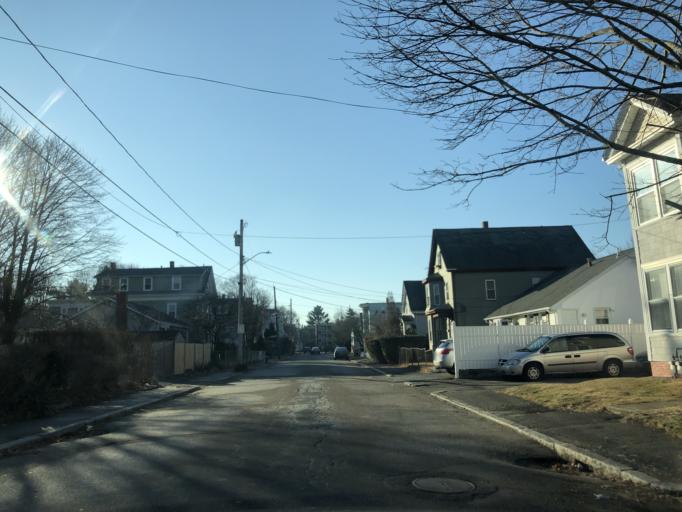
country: US
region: Massachusetts
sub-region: Plymouth County
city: Brockton
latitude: 42.0994
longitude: -71.0254
